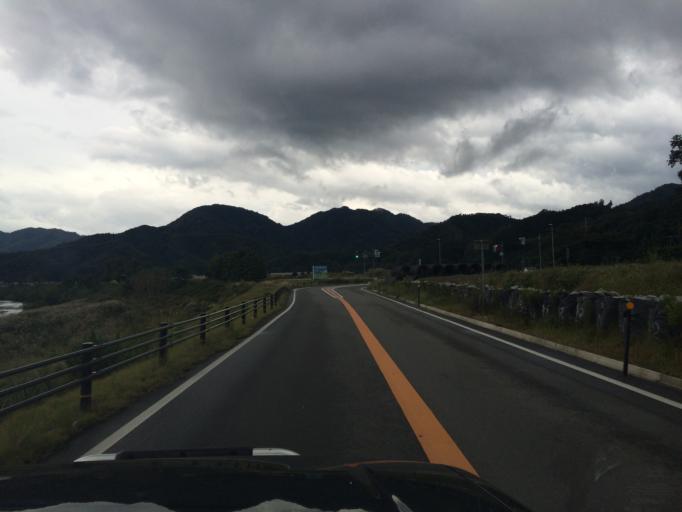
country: JP
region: Hyogo
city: Toyooka
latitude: 35.4488
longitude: 134.7713
